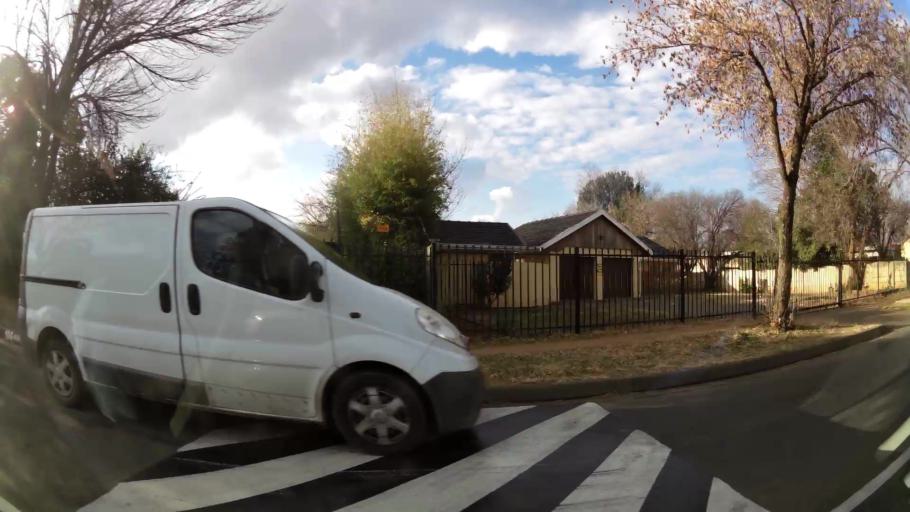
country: ZA
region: Orange Free State
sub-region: Mangaung Metropolitan Municipality
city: Bloemfontein
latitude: -29.1025
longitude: 26.1993
